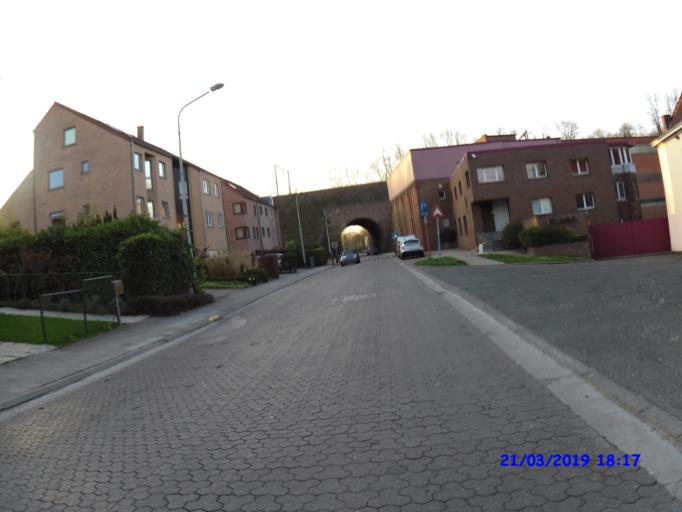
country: BE
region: Flanders
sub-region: Provincie Vlaams-Brabant
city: Linkebeek
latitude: 50.7767
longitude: 4.3297
